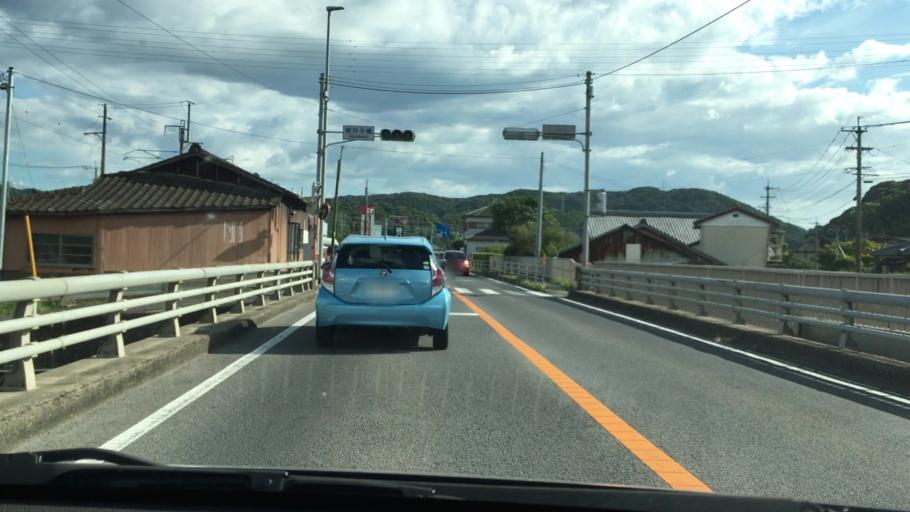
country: JP
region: Nagasaki
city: Sasebo
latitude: 33.1480
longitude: 129.8282
